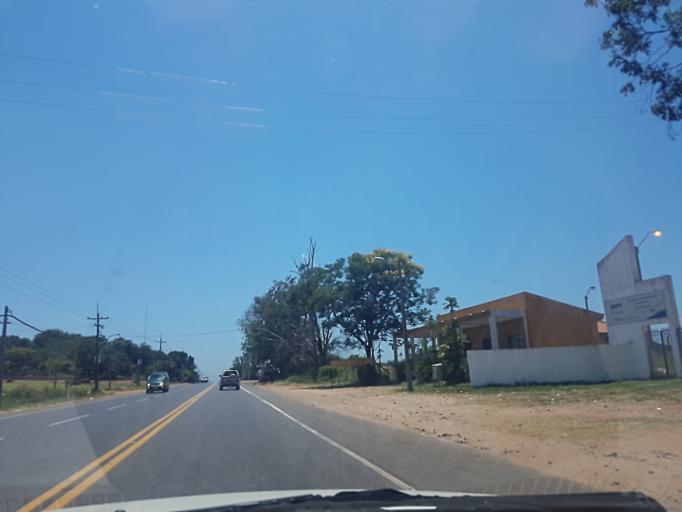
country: PY
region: Cordillera
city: Eusebio Ayala
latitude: -25.3836
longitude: -57.0499
